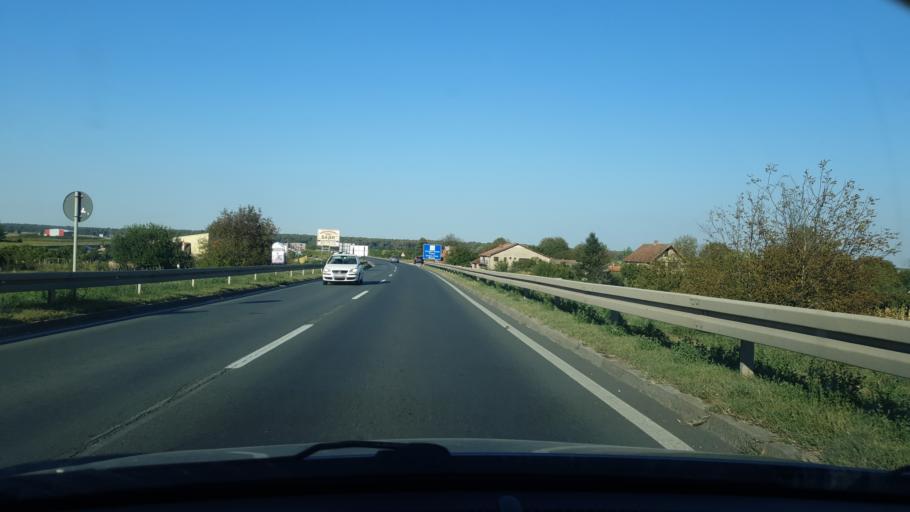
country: RS
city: Klenak
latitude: 44.7600
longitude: 19.7202
